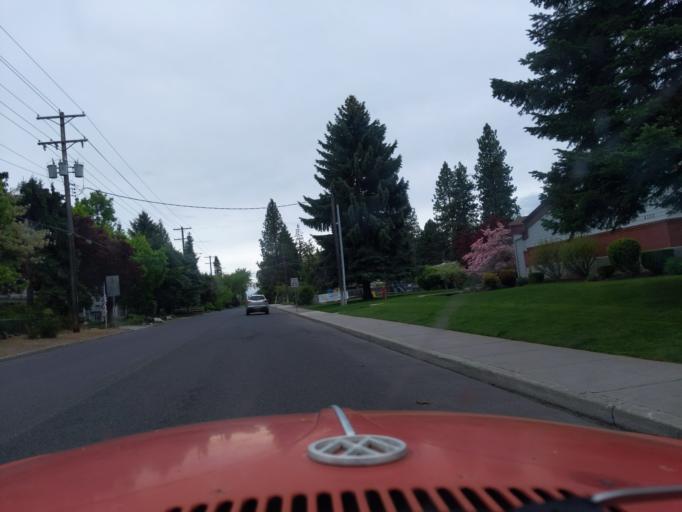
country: US
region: Washington
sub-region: Spokane County
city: Spokane
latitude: 47.6172
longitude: -117.3793
